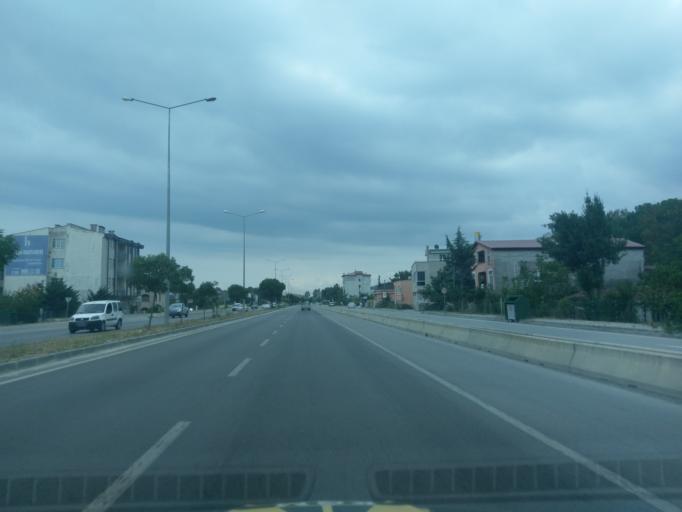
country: TR
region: Samsun
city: Taflan
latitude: 41.3987
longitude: 36.1939
